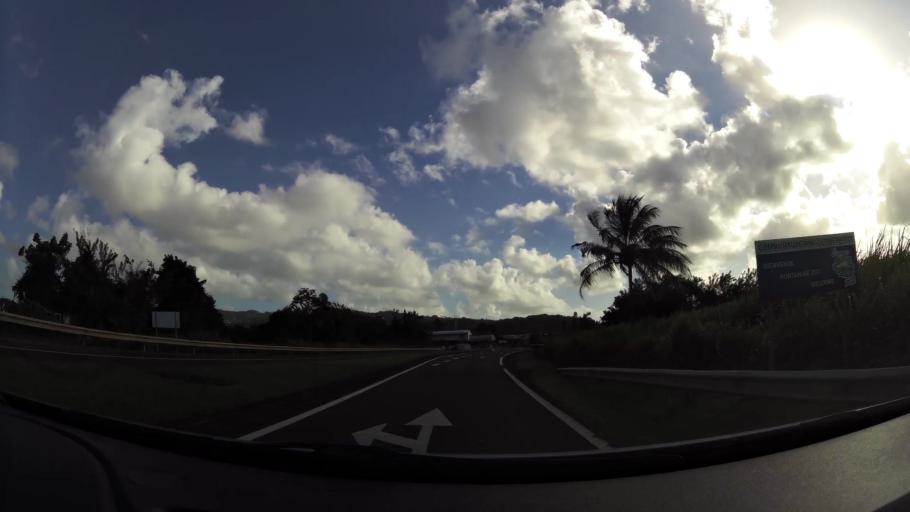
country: MQ
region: Martinique
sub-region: Martinique
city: Ducos
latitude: 14.5998
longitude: -60.9740
